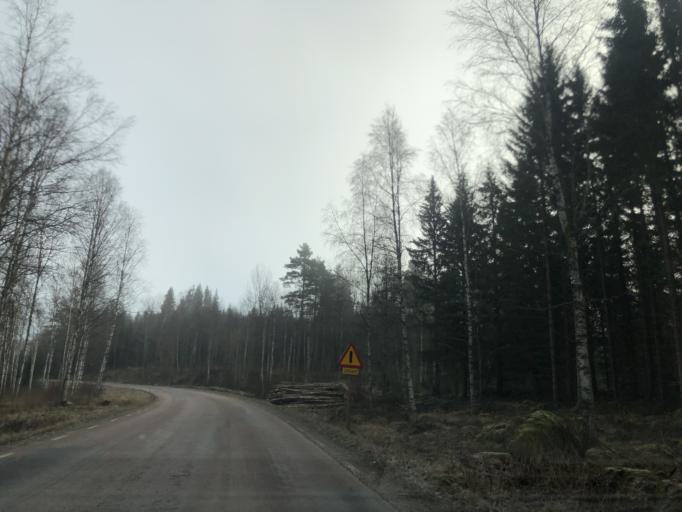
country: SE
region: Vaestra Goetaland
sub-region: Ulricehamns Kommun
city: Ulricehamn
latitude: 57.8272
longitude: 13.4478
